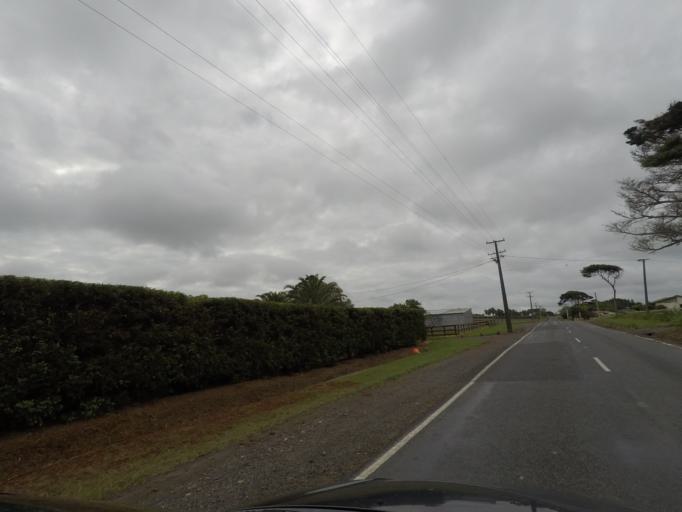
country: NZ
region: Auckland
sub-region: Auckland
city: Rosebank
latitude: -36.8073
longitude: 174.5761
